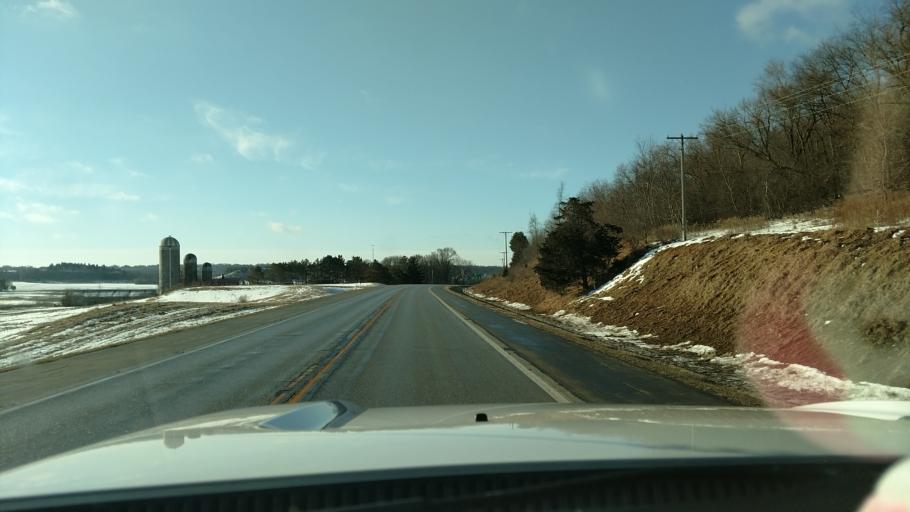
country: US
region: Minnesota
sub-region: Olmsted County
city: Rochester
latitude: 44.1137
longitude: -92.4281
